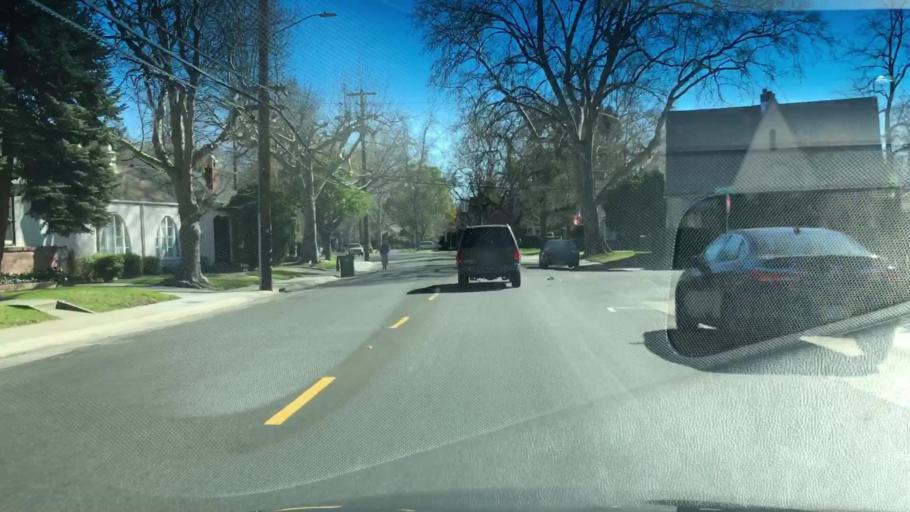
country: US
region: California
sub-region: Sacramento County
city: Sacramento
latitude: 38.5554
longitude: -121.4896
